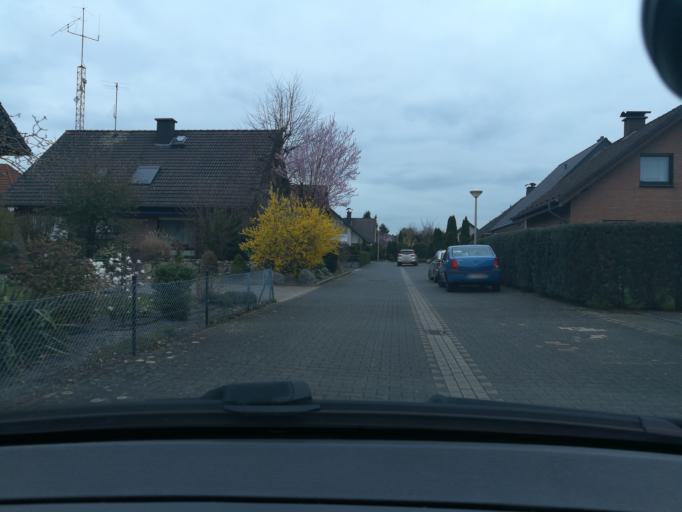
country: DE
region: North Rhine-Westphalia
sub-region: Regierungsbezirk Detmold
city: Oerlinghausen
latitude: 51.9351
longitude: 8.6343
